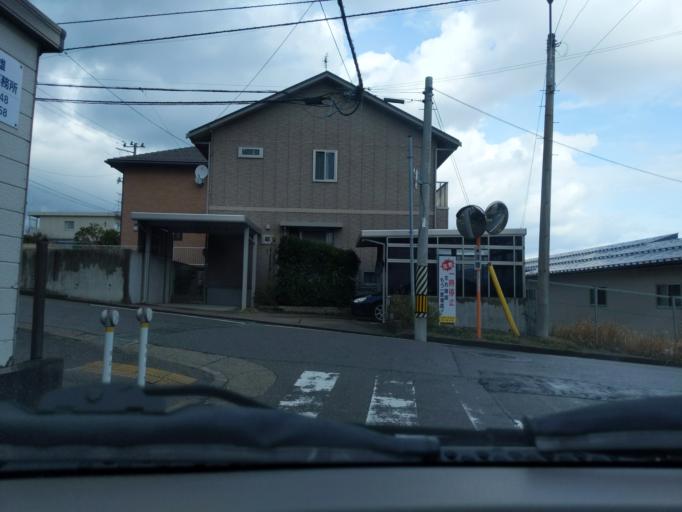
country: JP
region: Niigata
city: Niigata-shi
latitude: 37.9321
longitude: 139.0431
